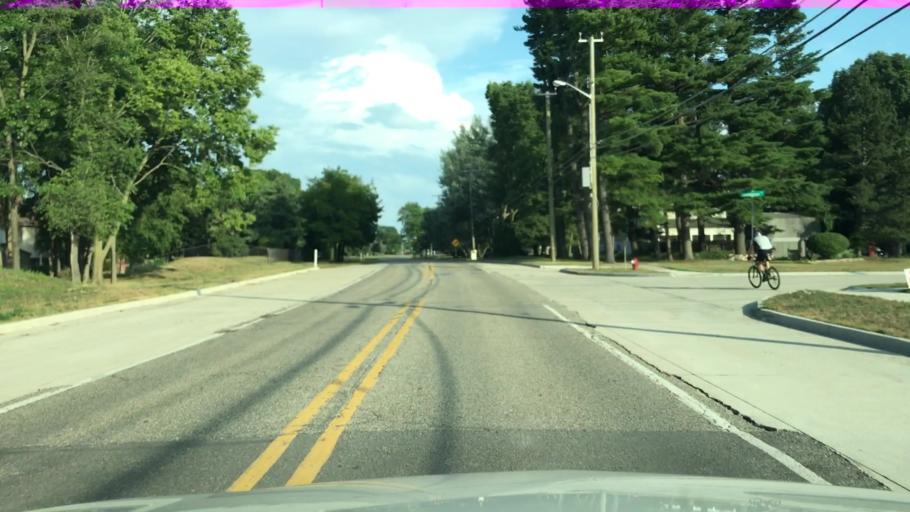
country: US
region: Michigan
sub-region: Macomb County
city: Fraser
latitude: 42.5836
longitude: -82.9766
